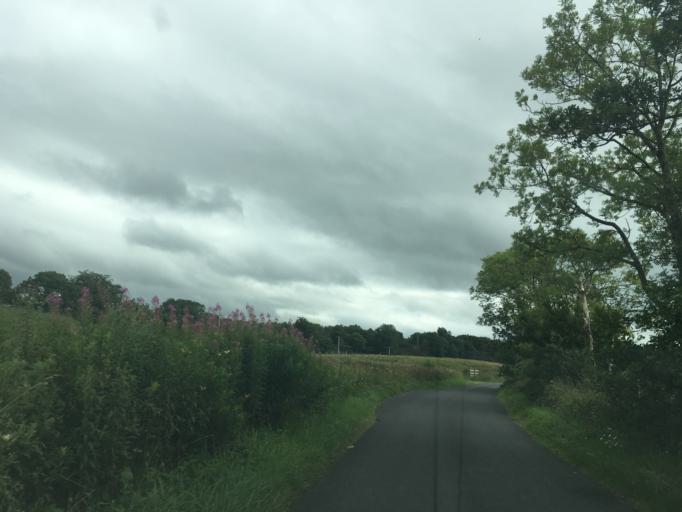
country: GB
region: Scotland
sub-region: Argyll and Bute
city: Lochgilphead
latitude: 56.1127
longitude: -5.4921
